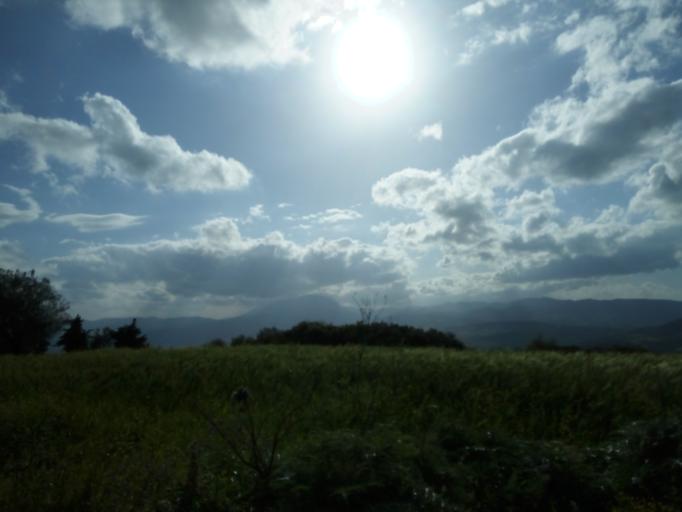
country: DZ
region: Tipaza
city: El Affroun
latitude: 36.3752
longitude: 2.5160
